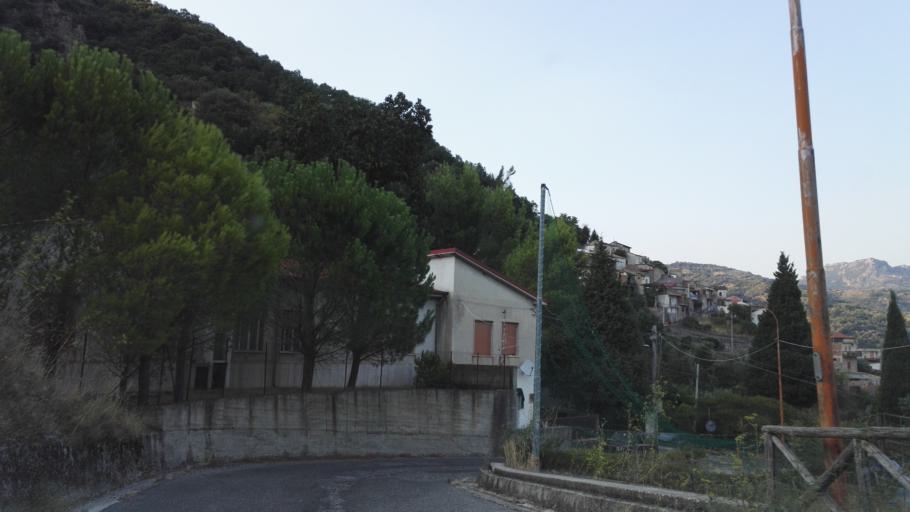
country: IT
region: Calabria
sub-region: Provincia di Reggio Calabria
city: Caulonia
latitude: 38.4147
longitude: 16.3725
